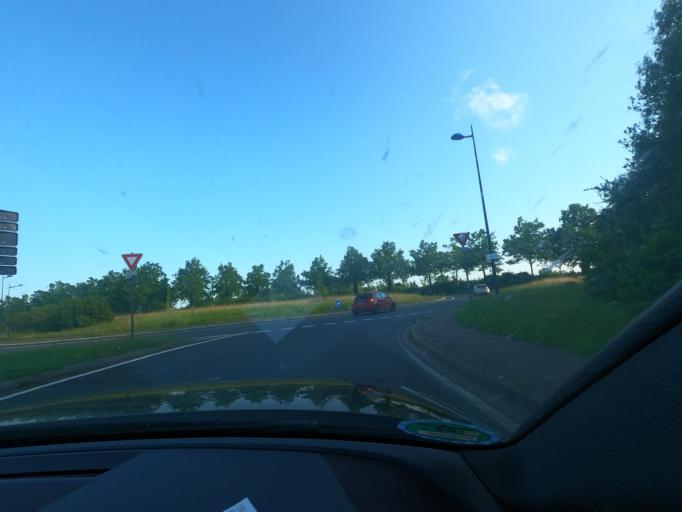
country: FR
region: Picardie
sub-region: Departement de la Somme
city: Pont-de-Metz
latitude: 49.9003
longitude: 2.2644
